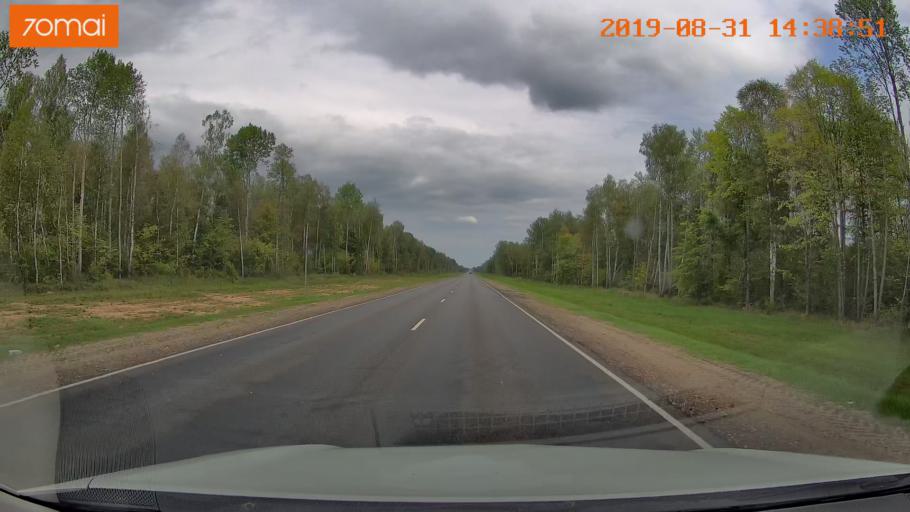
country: RU
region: Smolensk
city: Yekimovichi
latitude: 54.1874
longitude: 33.5383
